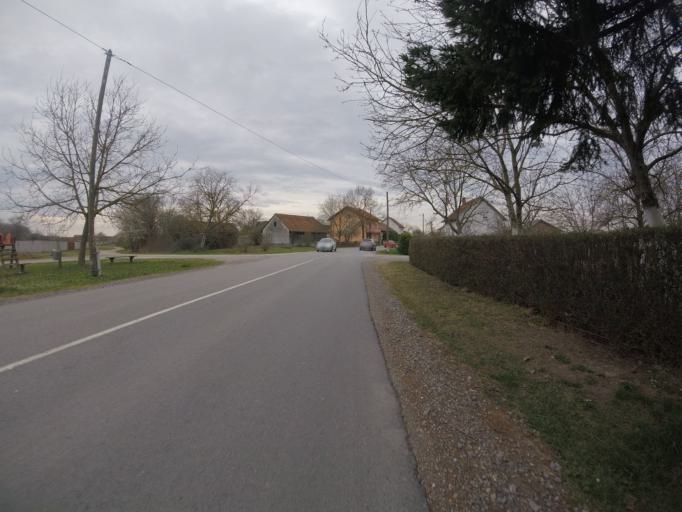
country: HR
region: Grad Zagreb
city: Odra
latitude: 45.7118
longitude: 16.0177
